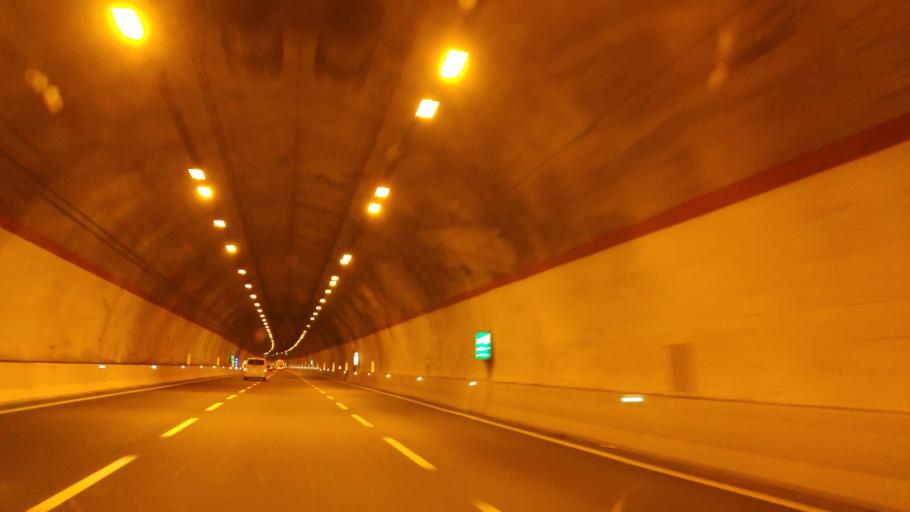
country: IT
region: Campania
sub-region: Provincia di Salerno
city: Contursi Terme
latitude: 40.6220
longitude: 15.2422
